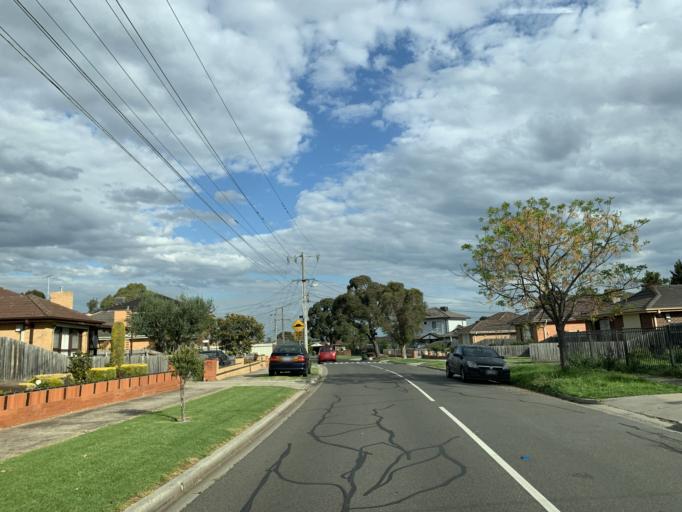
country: AU
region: Victoria
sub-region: Brimbank
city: Albion
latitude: -37.7559
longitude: 144.8528
